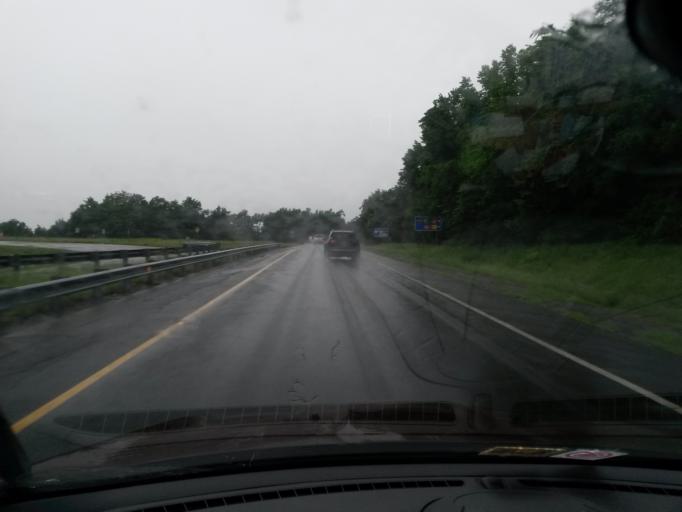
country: US
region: Virginia
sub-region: Henrico County
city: Chamberlayne
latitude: 37.6601
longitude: -77.4586
